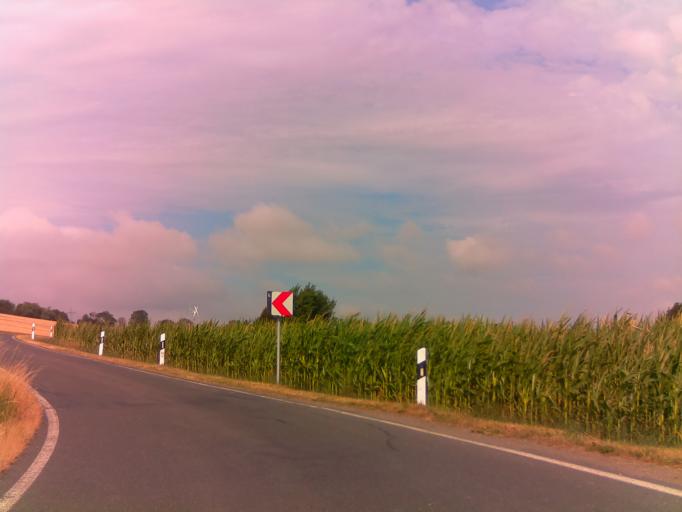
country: DE
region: Thuringia
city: Altenbeuthen
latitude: 50.5560
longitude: 11.6033
